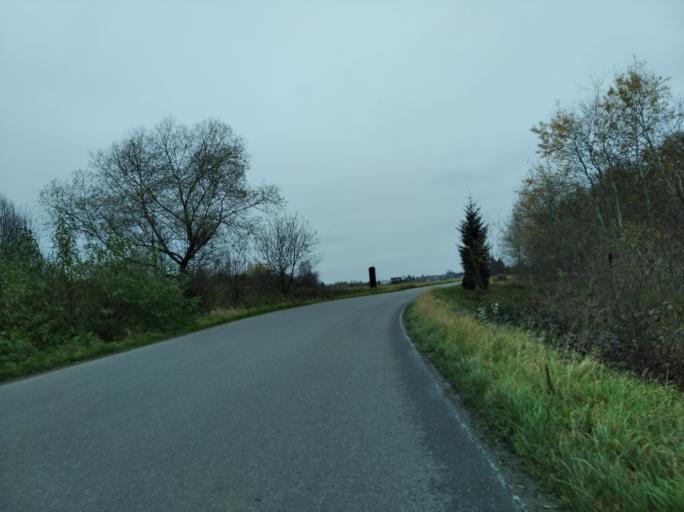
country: PL
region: Subcarpathian Voivodeship
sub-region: Powiat krosnienski
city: Chorkowka
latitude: 49.6767
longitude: 21.6803
